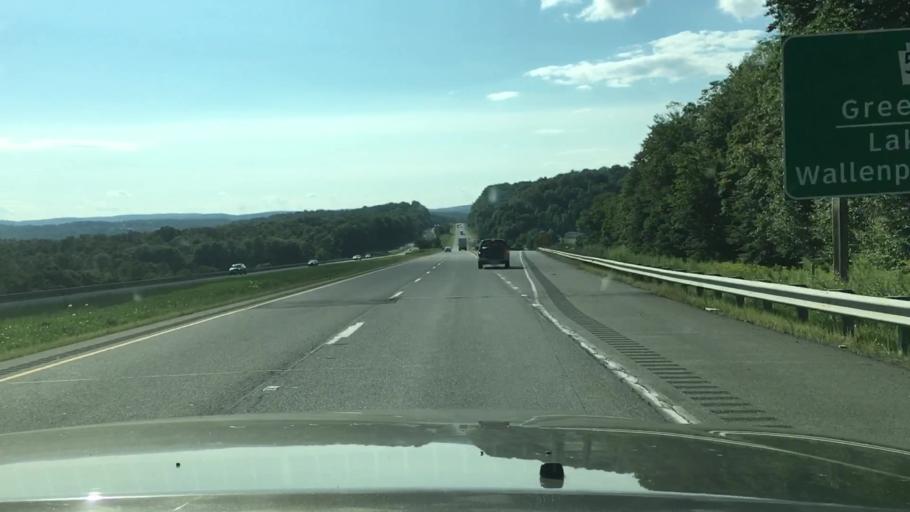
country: US
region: Pennsylvania
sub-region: Monroe County
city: Mountainhome
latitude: 41.3406
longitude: -75.3079
